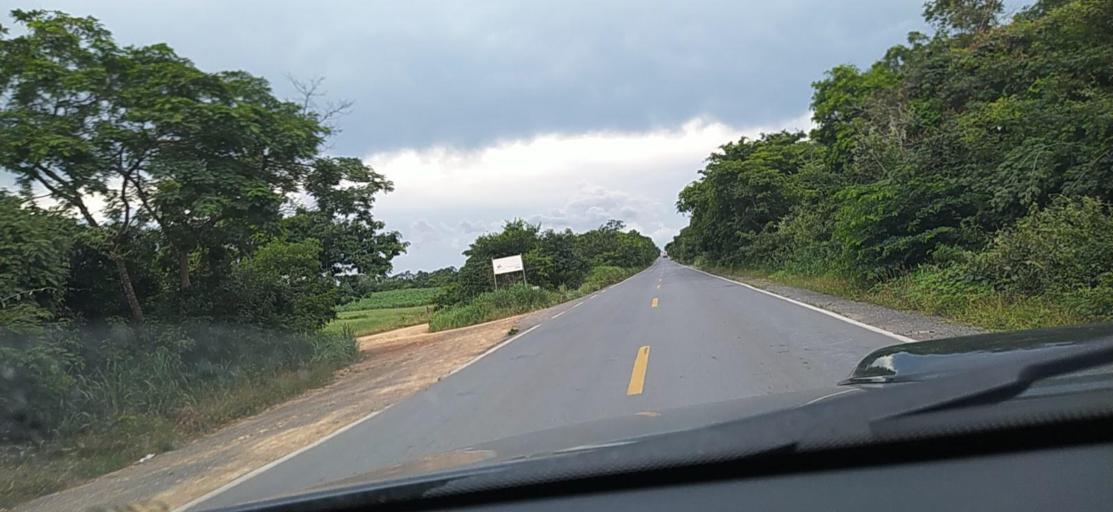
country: BR
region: Minas Gerais
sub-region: Francisco Sa
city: Francisco Sa
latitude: -16.2453
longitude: -43.6269
